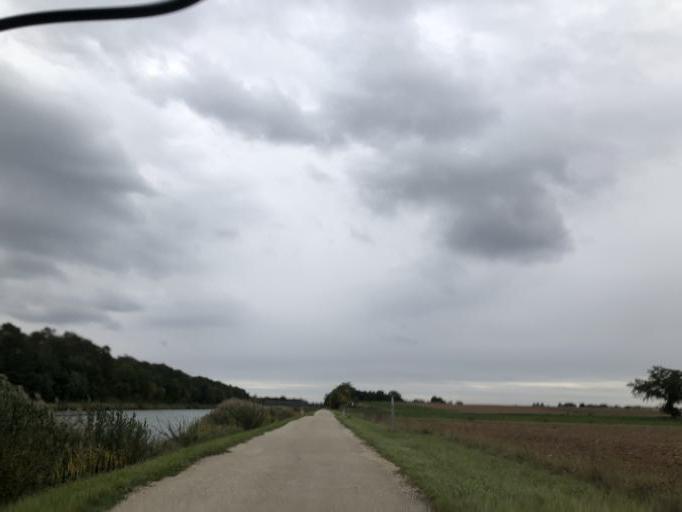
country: DE
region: Bavaria
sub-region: Regierungsbezirk Mittelfranken
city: Erlangen
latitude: 49.5483
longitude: 10.9688
